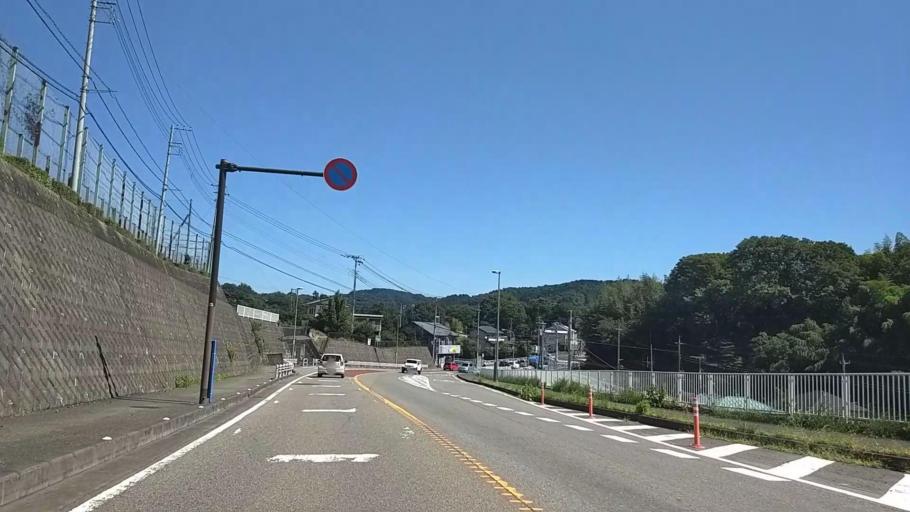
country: JP
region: Tokyo
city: Hachioji
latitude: 35.5654
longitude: 139.2605
